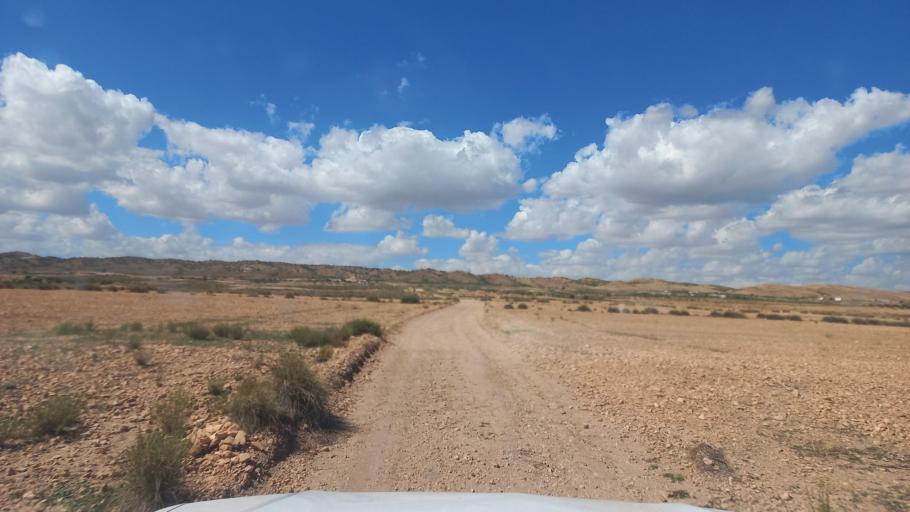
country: TN
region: Al Qasrayn
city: Sbiba
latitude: 35.3572
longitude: 9.0095
